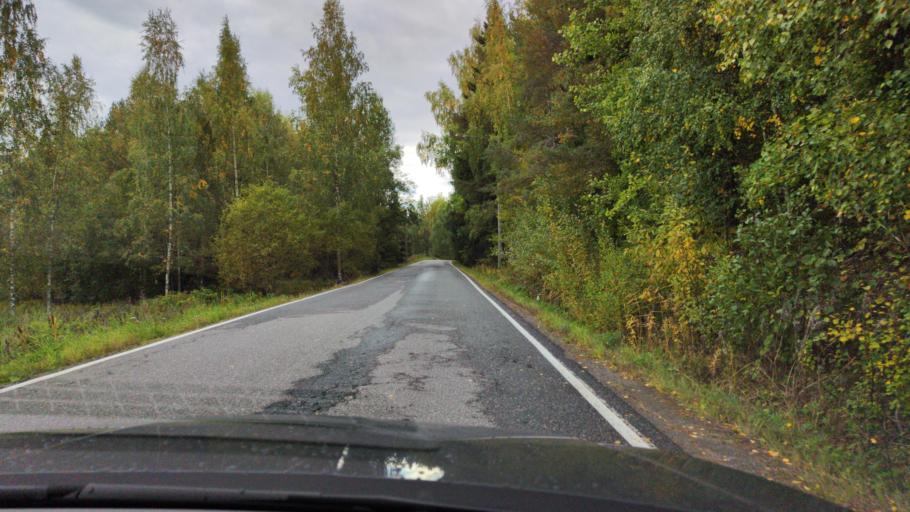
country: FI
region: Varsinais-Suomi
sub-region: Aboland-Turunmaa
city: Pargas
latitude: 60.3715
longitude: 22.2765
